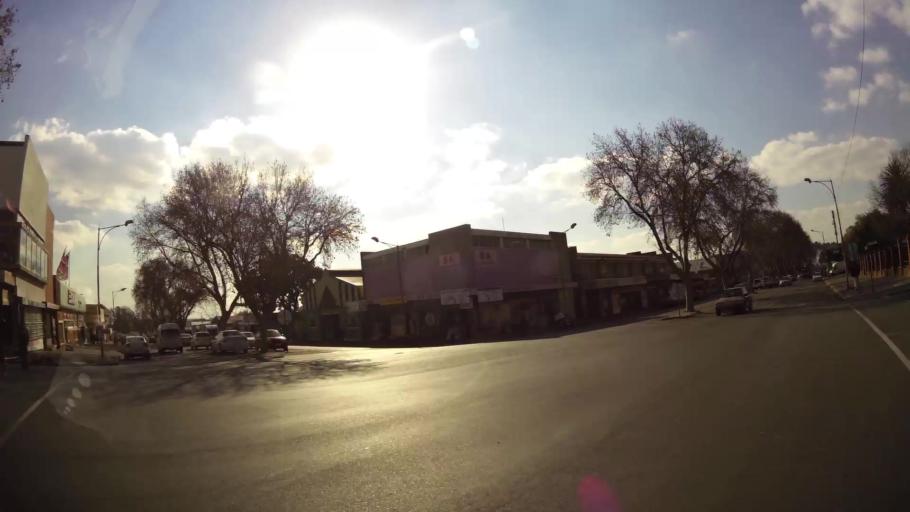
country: ZA
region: Gauteng
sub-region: West Rand District Municipality
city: Krugersdorp
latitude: -26.0993
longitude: 27.7720
